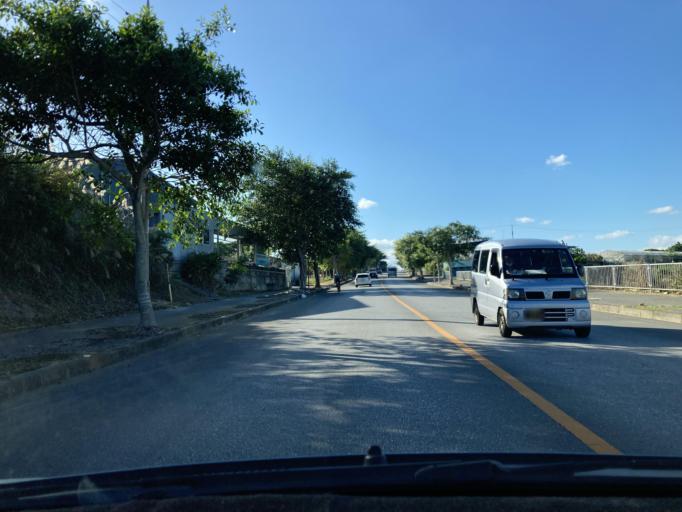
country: JP
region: Okinawa
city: Gushikawa
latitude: 26.3685
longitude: 127.8358
